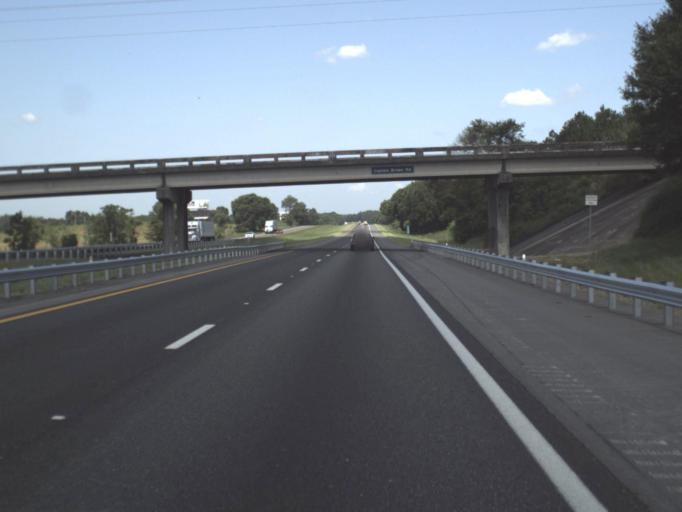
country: US
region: Florida
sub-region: Madison County
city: Madison
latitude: 30.4358
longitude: -83.4961
